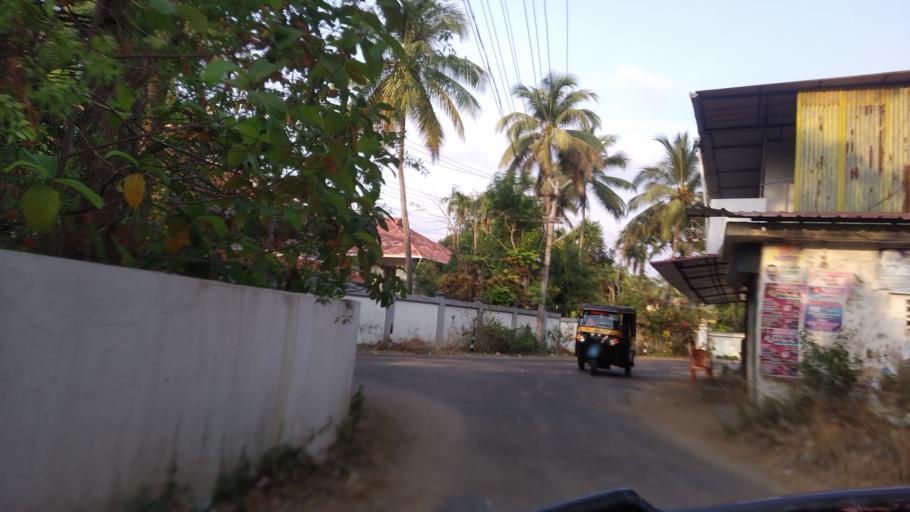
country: IN
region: Kerala
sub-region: Thrissur District
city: Thanniyam
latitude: 10.4102
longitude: 76.0937
